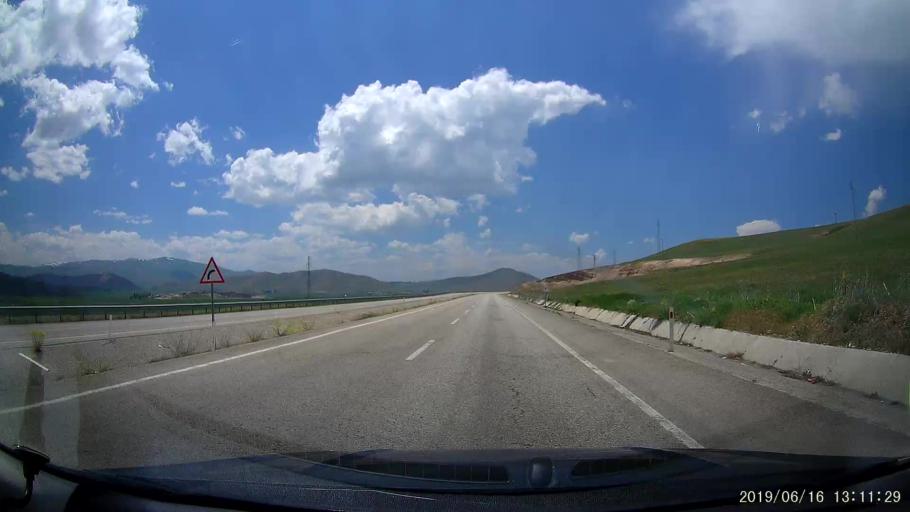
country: TR
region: Agri
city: Diyadin
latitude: 39.5919
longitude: 43.6064
